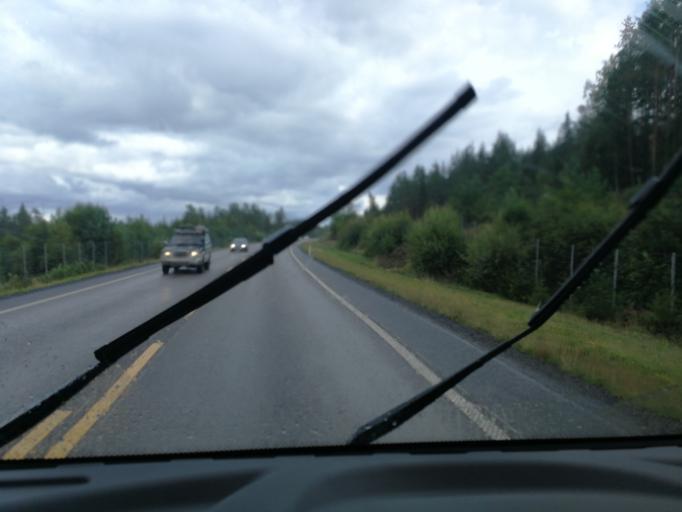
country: NO
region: Ostfold
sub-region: Marker
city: Orje
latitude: 59.5349
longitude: 11.5619
